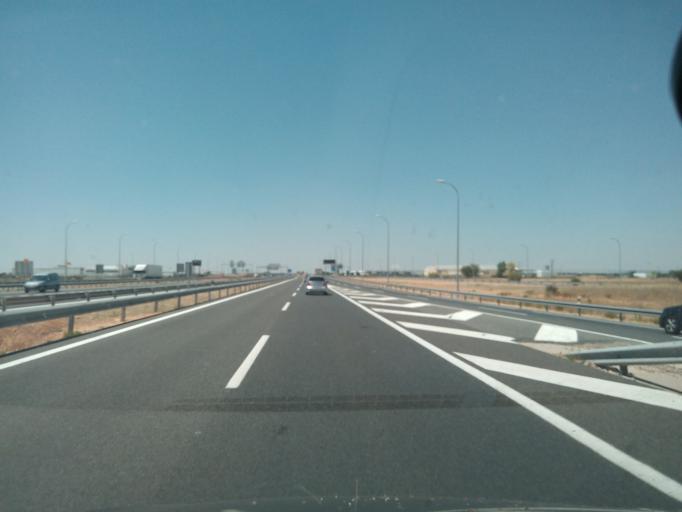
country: ES
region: Castille-La Mancha
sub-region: Province of Toledo
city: Ocana
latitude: 39.9263
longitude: -3.4828
